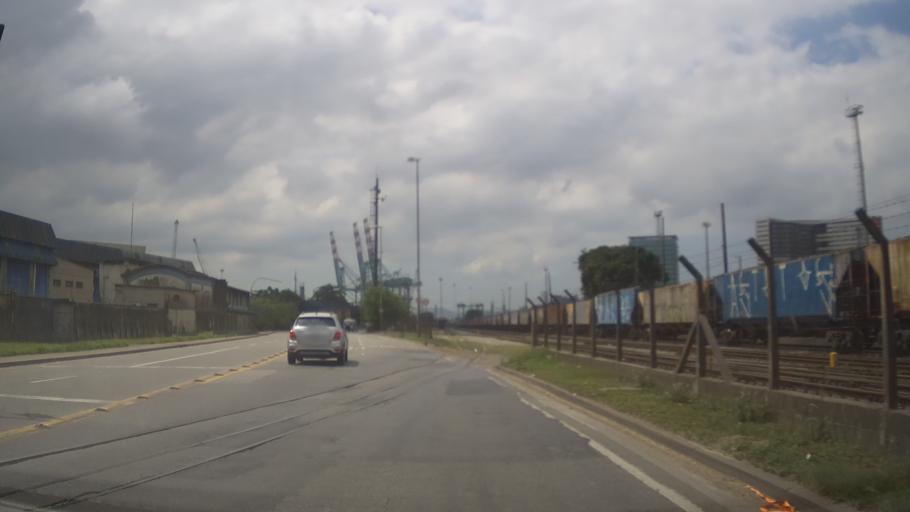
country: BR
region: Sao Paulo
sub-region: Santos
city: Santos
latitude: -23.9276
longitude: -46.3421
